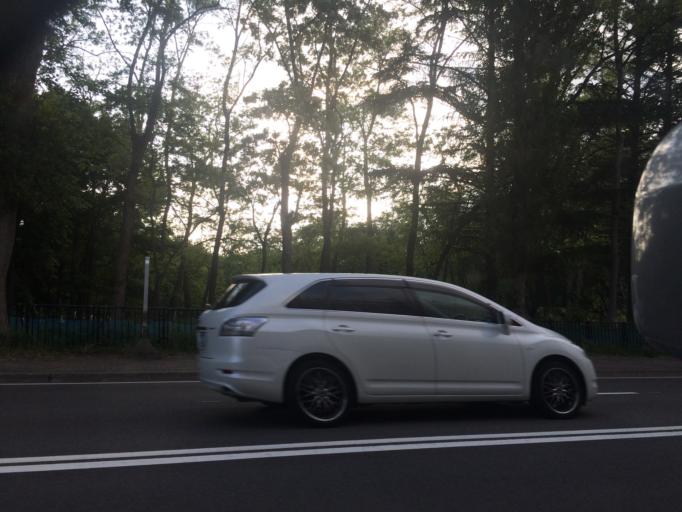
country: JP
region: Hokkaido
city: Sapporo
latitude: 42.9957
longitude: 141.3493
